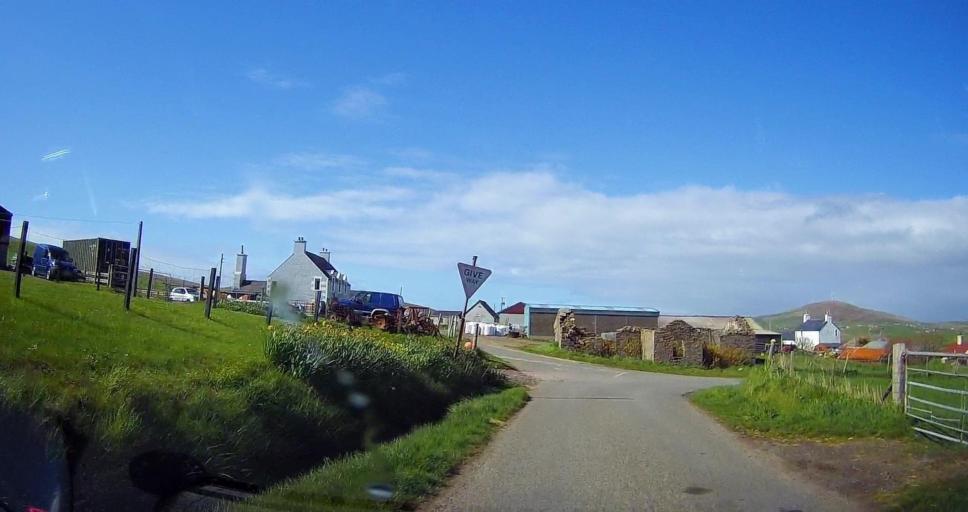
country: GB
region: Scotland
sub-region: Shetland Islands
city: Sandwick
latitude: 59.9095
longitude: -1.3346
